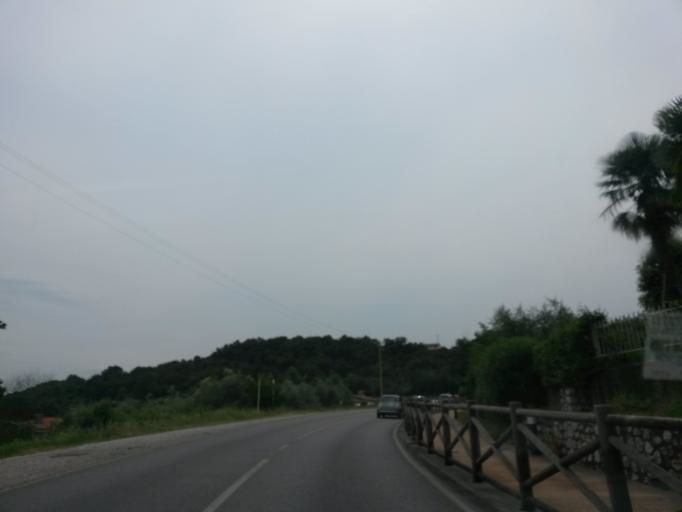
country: IT
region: Lombardy
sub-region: Provincia di Brescia
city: Cunettone-Villa
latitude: 45.5951
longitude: 10.5107
